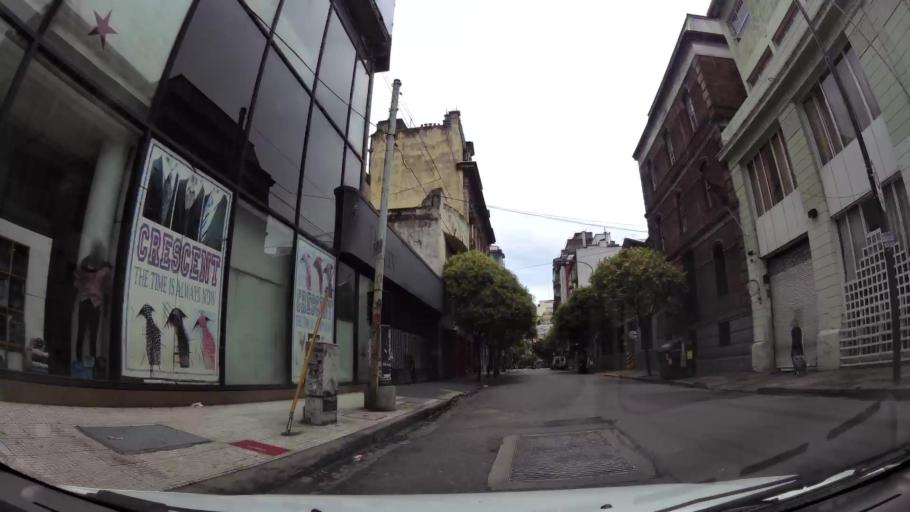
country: AR
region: Buenos Aires F.D.
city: Buenos Aires
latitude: -34.6034
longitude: -58.4053
